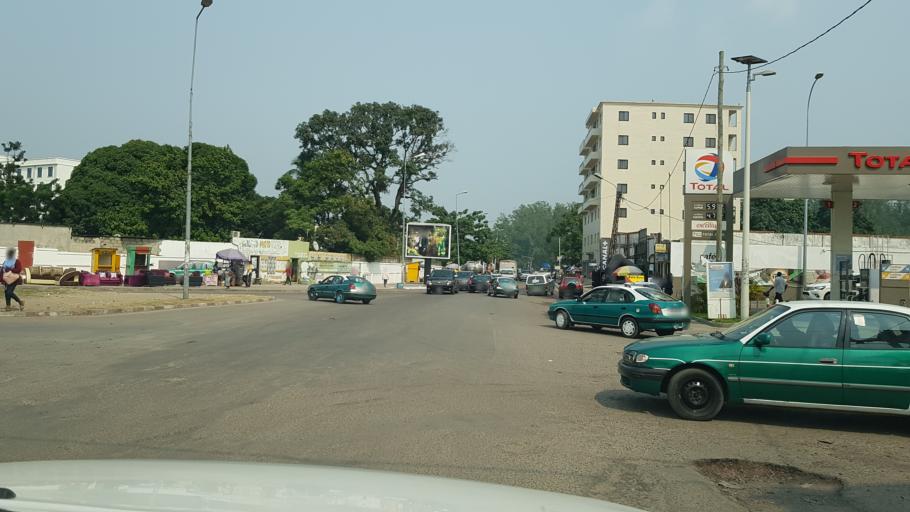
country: CG
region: Brazzaville
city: Brazzaville
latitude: -4.2615
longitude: 15.2605
